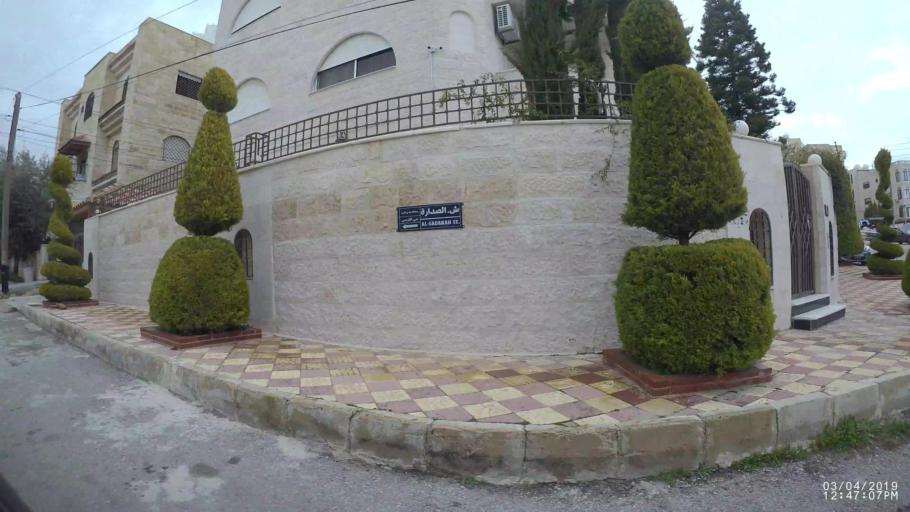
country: JO
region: Amman
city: Wadi as Sir
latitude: 31.9662
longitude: 35.8335
